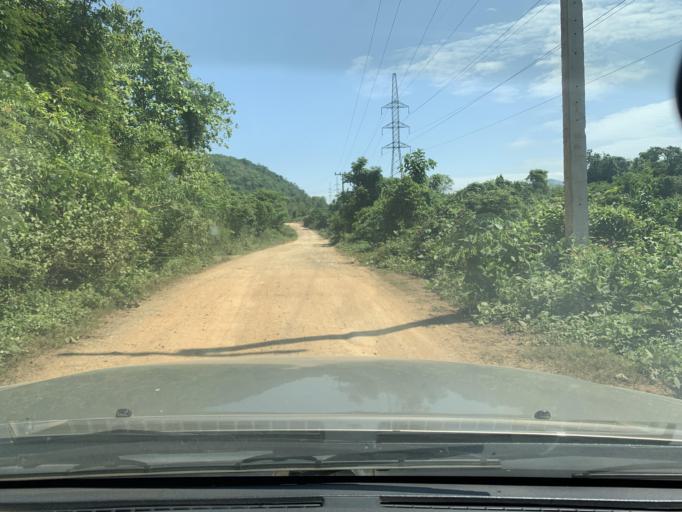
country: LA
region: Louangphabang
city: Louangphabang
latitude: 19.8941
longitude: 102.2075
